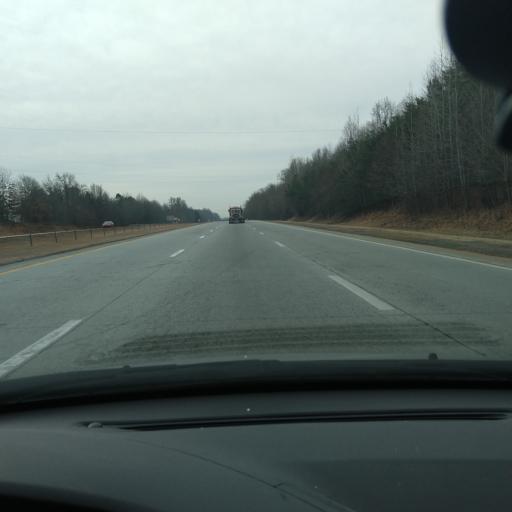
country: US
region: North Carolina
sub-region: Davidson County
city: Lexington
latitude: 35.8322
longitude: -80.2832
